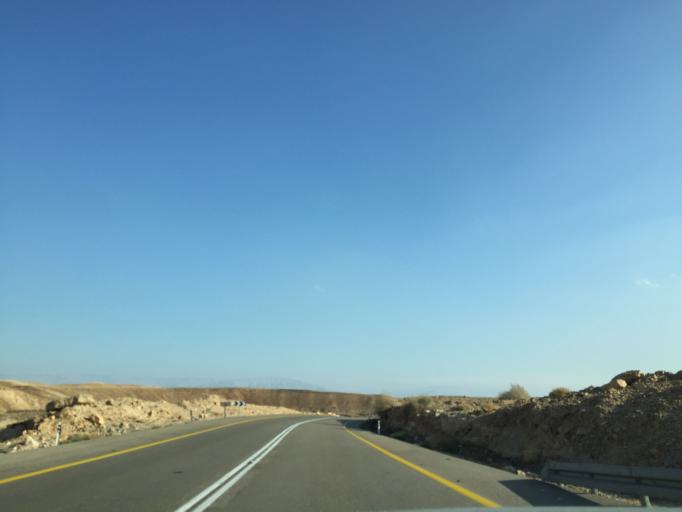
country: IL
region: Southern District
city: `En Boqeq
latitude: 31.1796
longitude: 35.2943
